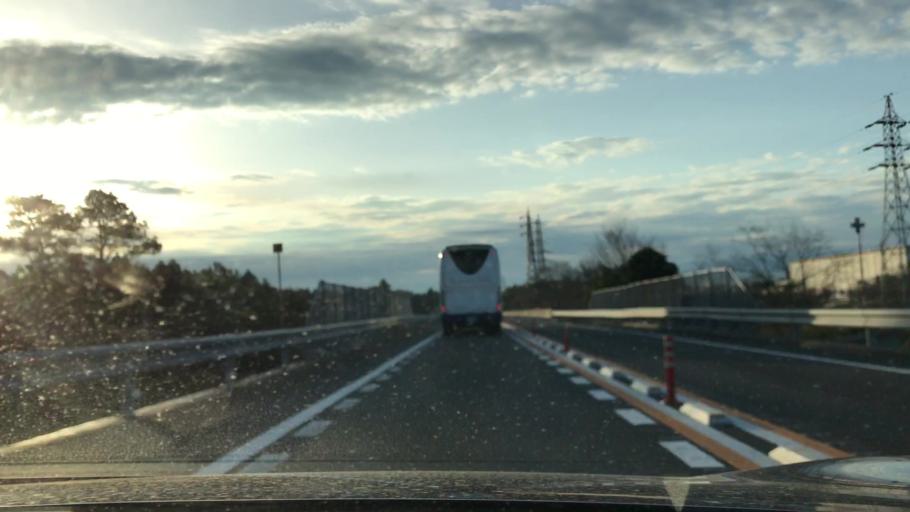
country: JP
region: Ibaraki
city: Ami
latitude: 35.9923
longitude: 140.2167
